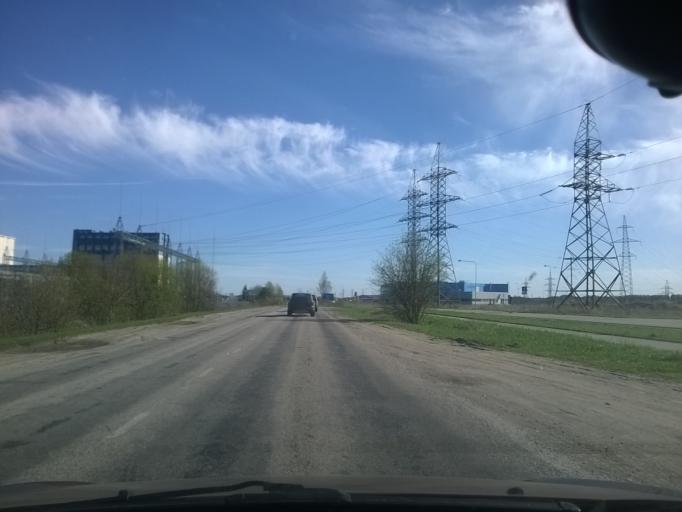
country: EE
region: Harju
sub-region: Joelaehtme vald
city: Loo
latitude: 59.4530
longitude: 24.9205
